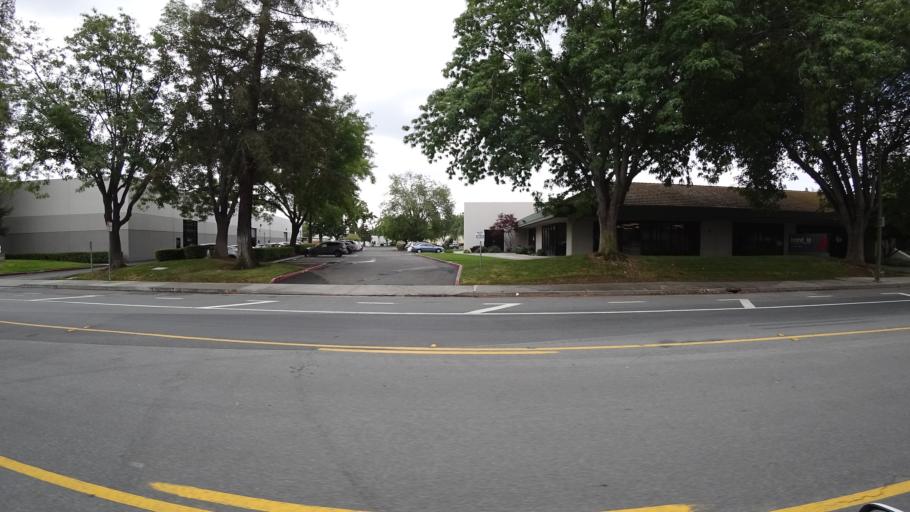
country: US
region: California
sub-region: Santa Clara County
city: Santa Clara
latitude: 37.3805
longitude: -121.9178
